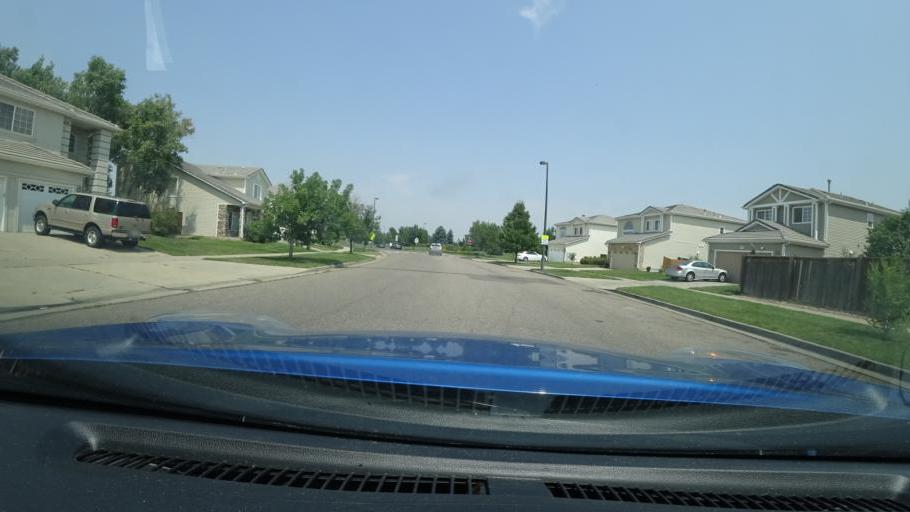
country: US
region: Colorado
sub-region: Adams County
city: Aurora
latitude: 39.7709
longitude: -104.7484
